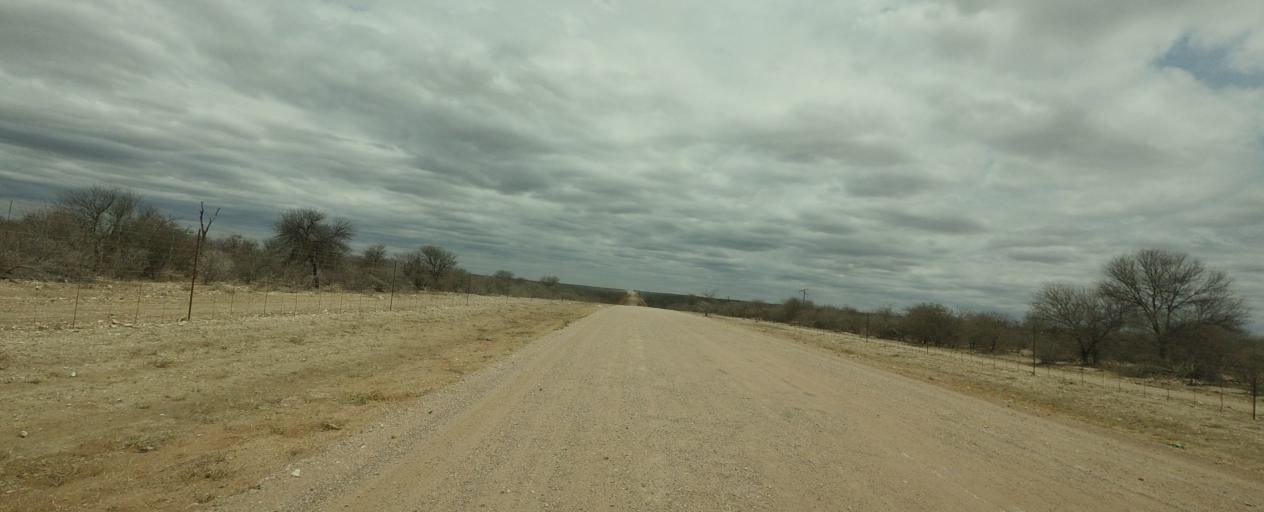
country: BW
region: Central
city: Mathathane
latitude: -22.6921
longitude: 28.6350
